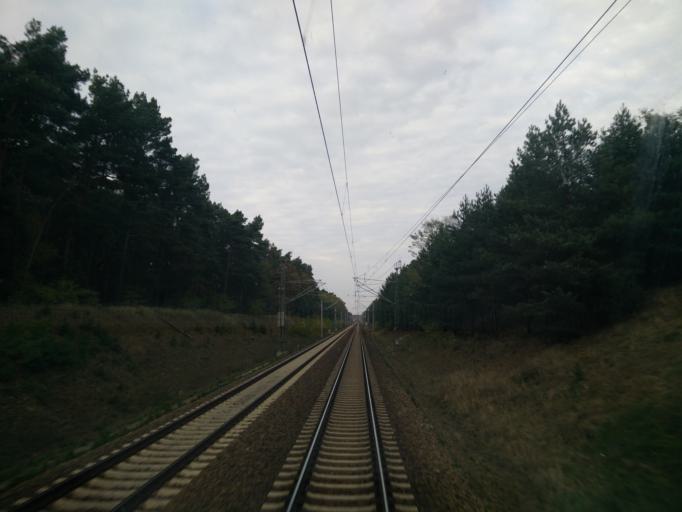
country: DE
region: Brandenburg
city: Halbe
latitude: 52.0398
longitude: 13.7190
